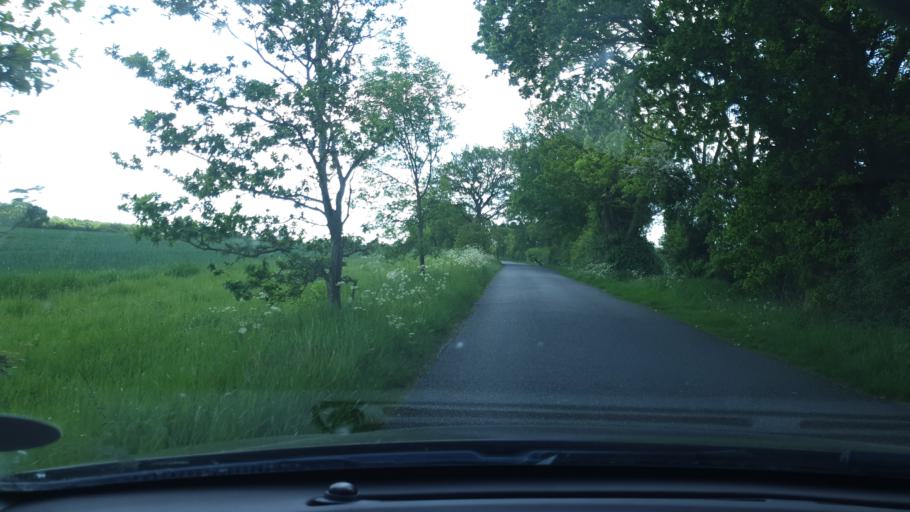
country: GB
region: England
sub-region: Essex
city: Great Bentley
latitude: 51.8481
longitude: 1.0885
